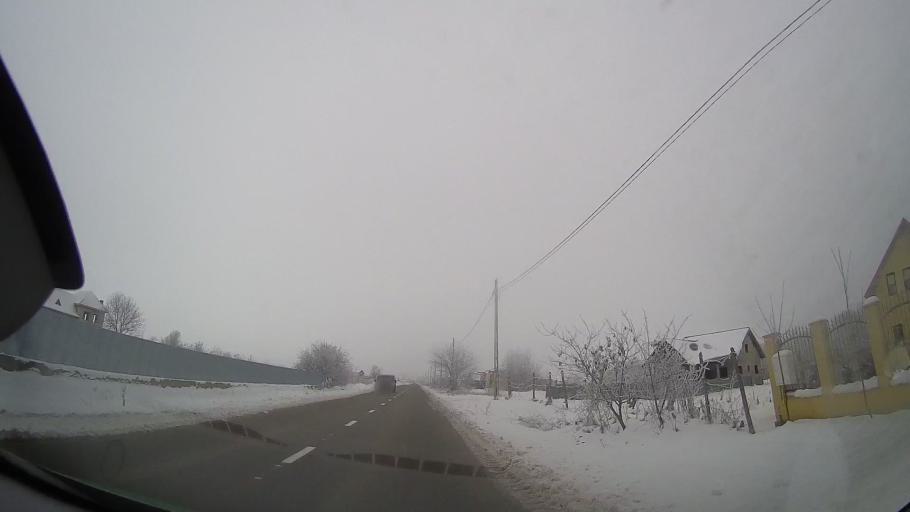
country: RO
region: Neamt
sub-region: Comuna Horia
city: Cotu Vames
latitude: 46.8895
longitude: 26.9660
